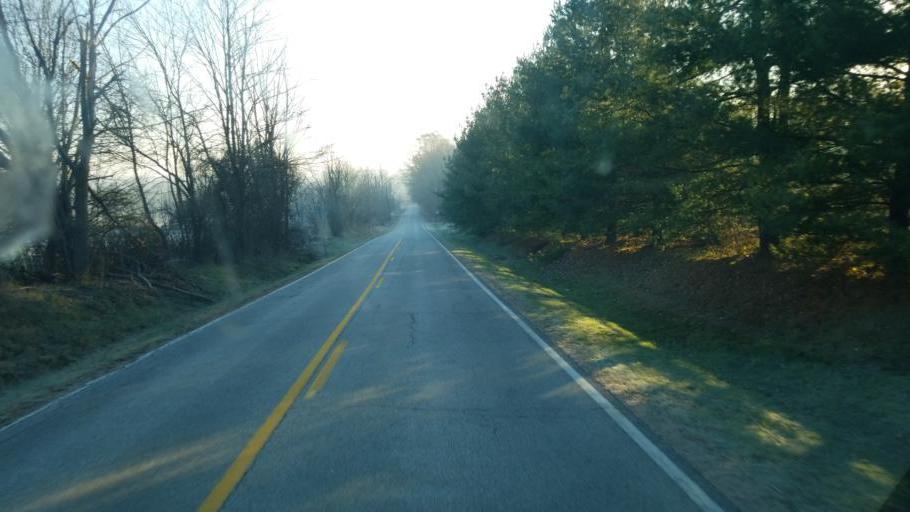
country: US
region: Ohio
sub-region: Medina County
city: Medina
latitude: 41.0916
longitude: -81.8122
